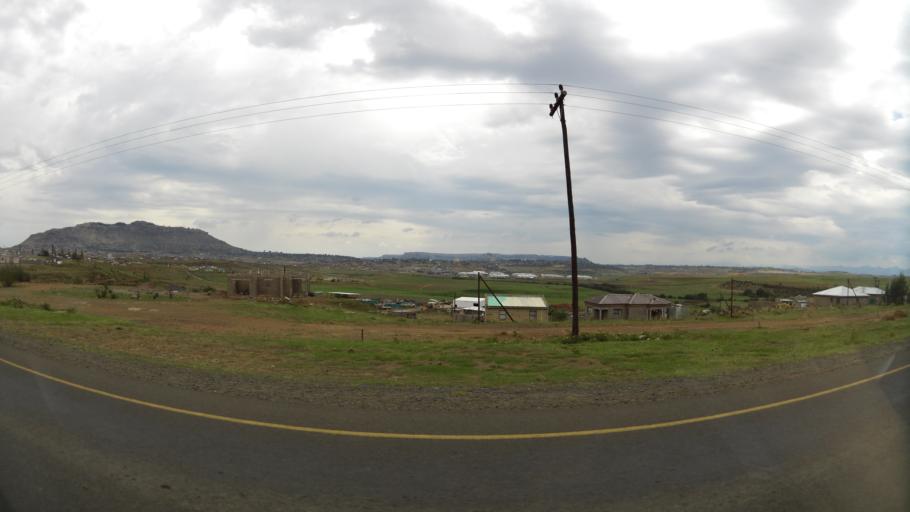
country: LS
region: Maseru
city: Maseru
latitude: -29.3901
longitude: 27.4715
